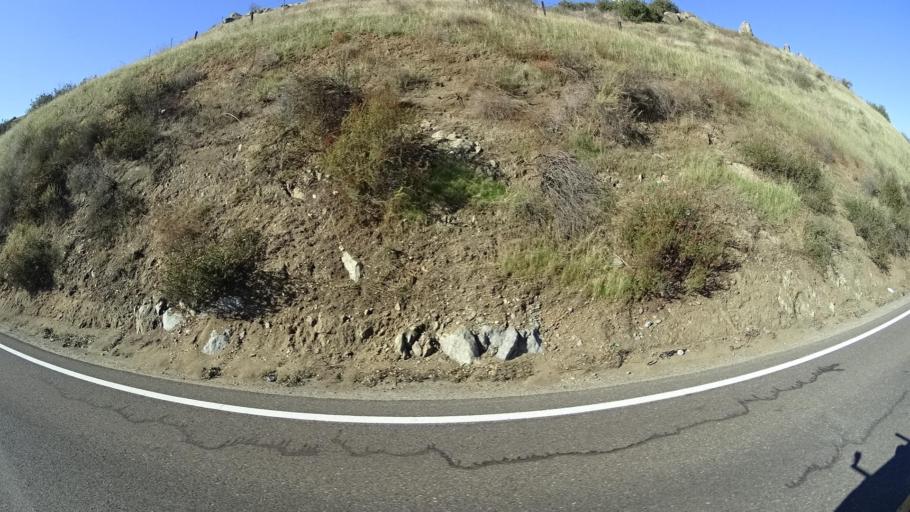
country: US
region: California
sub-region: San Diego County
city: Jamul
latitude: 32.6670
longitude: -116.8218
